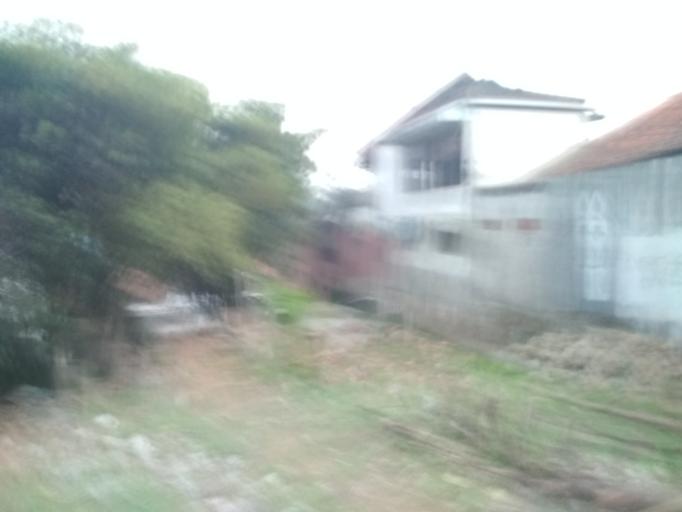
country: ID
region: West Java
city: Caringin
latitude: -6.7047
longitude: 106.8228
